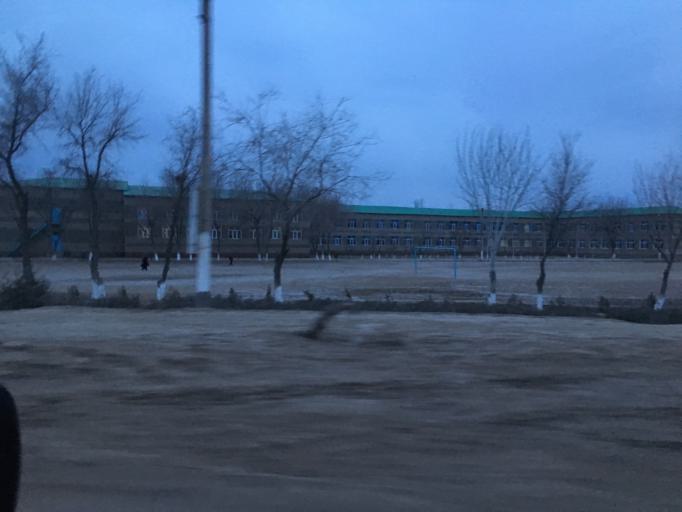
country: TM
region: Dasoguz
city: Yylanly
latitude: 41.8822
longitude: 59.6251
